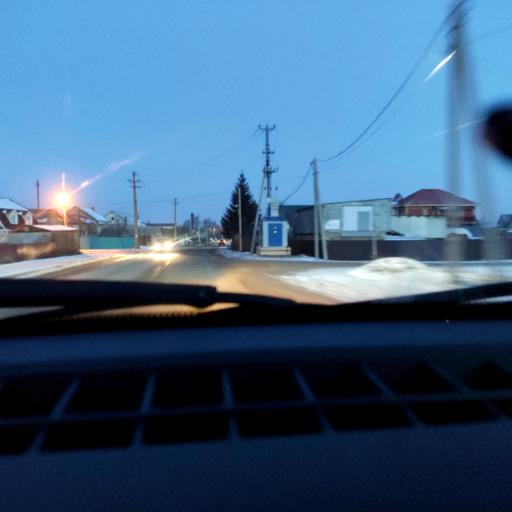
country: RU
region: Bashkortostan
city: Ufa
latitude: 54.6074
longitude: 55.9428
